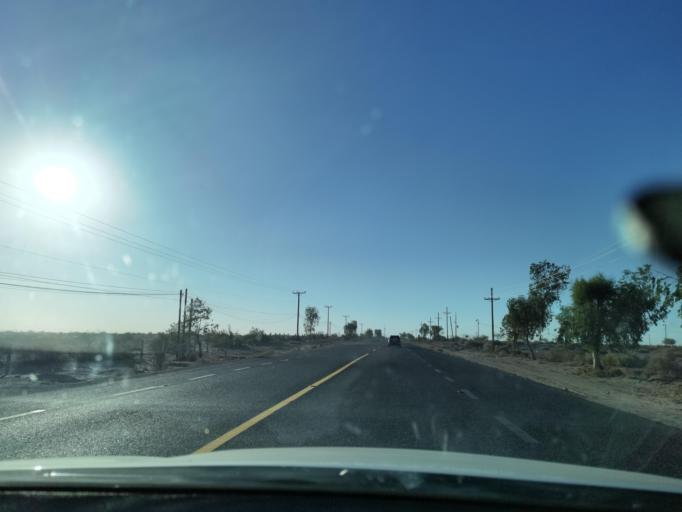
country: MX
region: Baja California
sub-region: Mexicali
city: Islas Agrarias Grupo A
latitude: 32.6336
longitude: -115.2722
